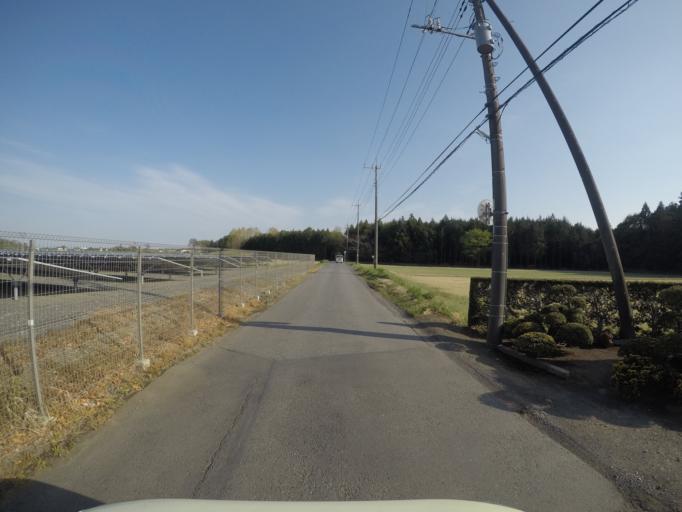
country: JP
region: Ibaraki
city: Ishige
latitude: 36.1601
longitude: 140.0154
